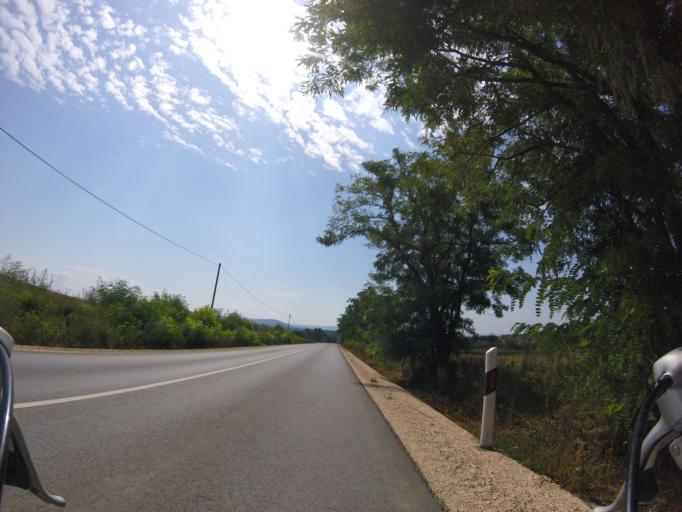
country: HU
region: Komarom-Esztergom
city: Kornye
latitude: 47.5573
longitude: 18.3320
